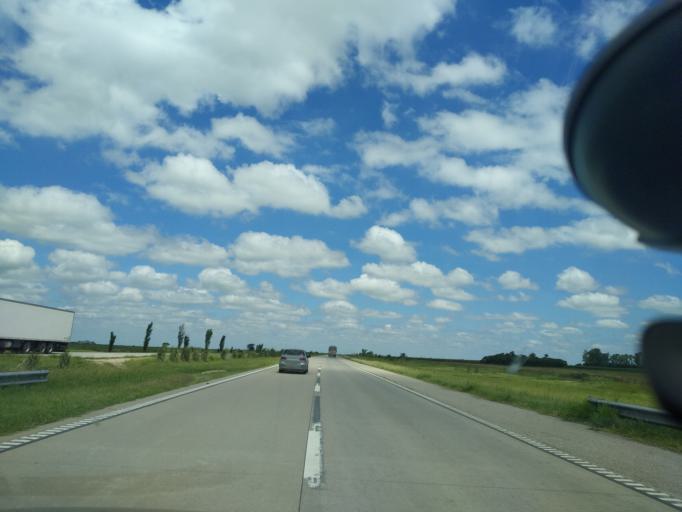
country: AR
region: Cordoba
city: Tio Pujio
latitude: -32.2842
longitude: -63.3040
